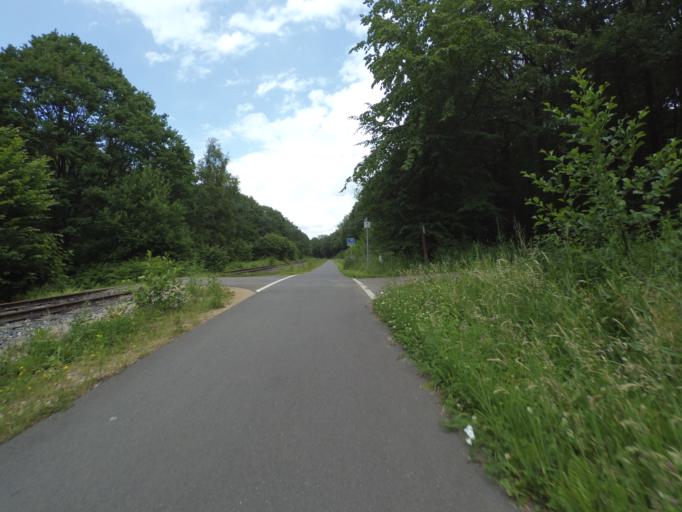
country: BE
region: Wallonia
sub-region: Province de Liege
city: Raeren
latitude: 50.6839
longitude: 6.1596
